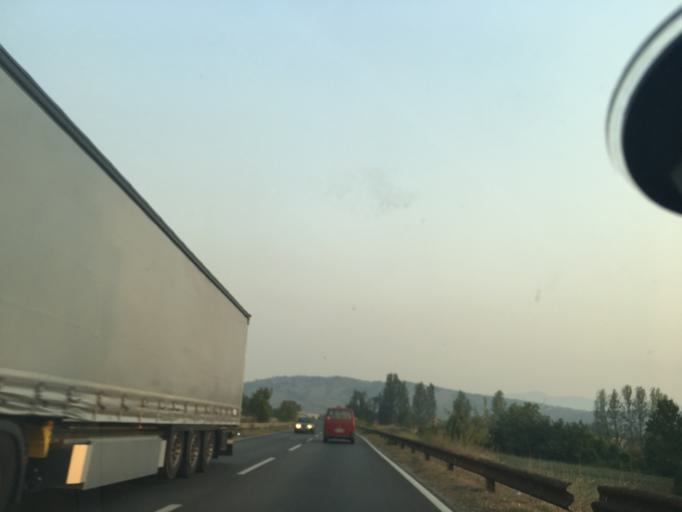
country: ME
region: Danilovgrad
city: Danilovgrad
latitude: 42.5204
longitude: 19.1212
